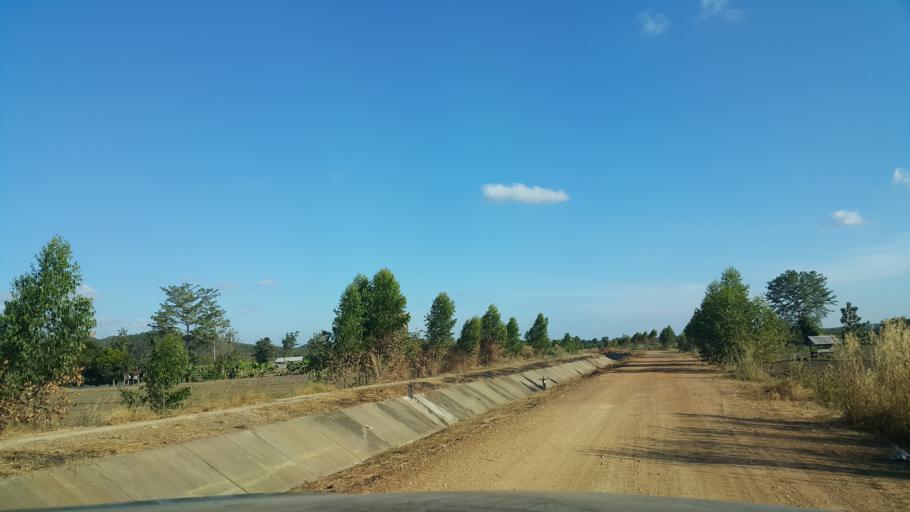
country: TH
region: Sukhothai
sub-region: Amphoe Si Satchanalai
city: Si Satchanalai
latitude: 17.4815
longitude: 99.6518
